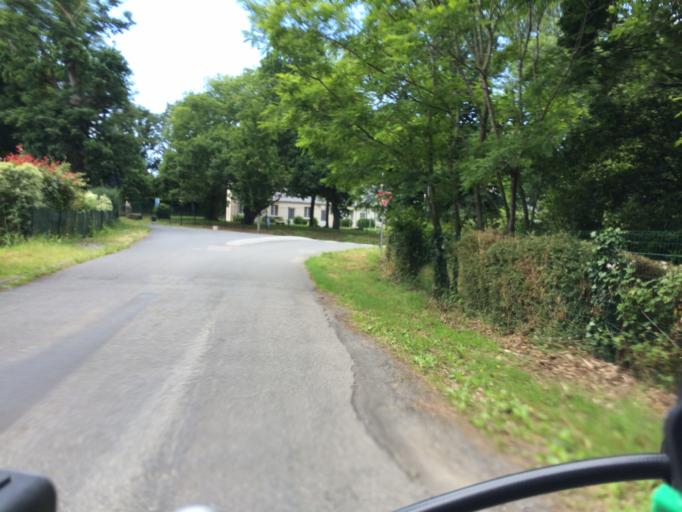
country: FR
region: Brittany
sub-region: Departement du Finistere
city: Logonna-Daoulas
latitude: 48.3214
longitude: -4.2864
